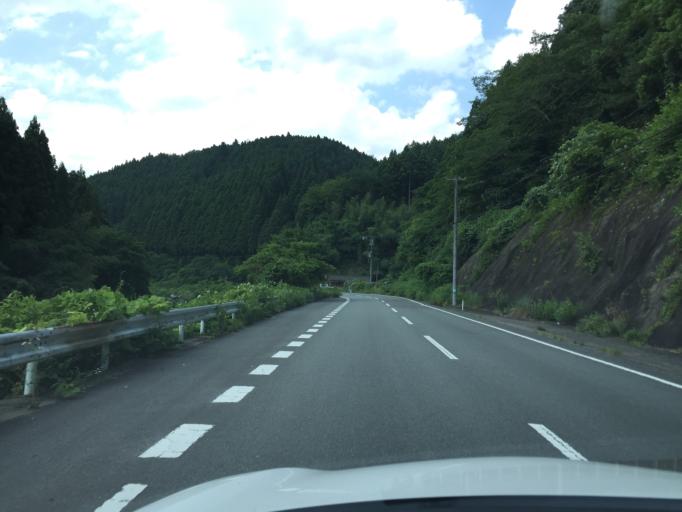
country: JP
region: Fukushima
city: Iwaki
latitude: 37.0065
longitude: 140.7189
